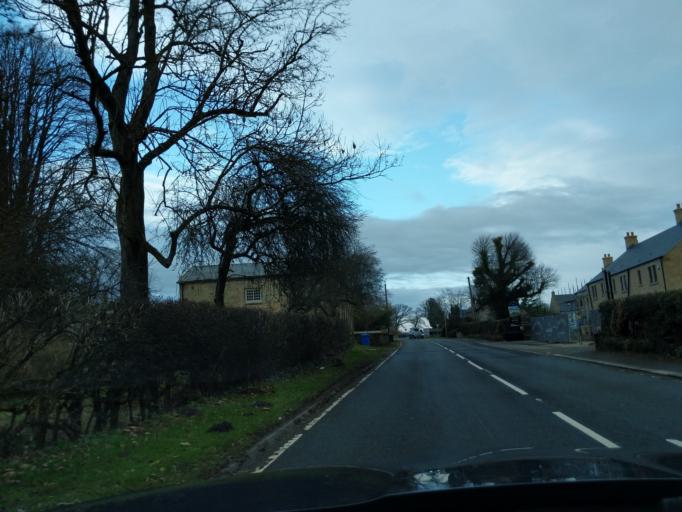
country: GB
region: England
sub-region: Northumberland
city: Meldon
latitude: 55.1046
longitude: -1.8434
